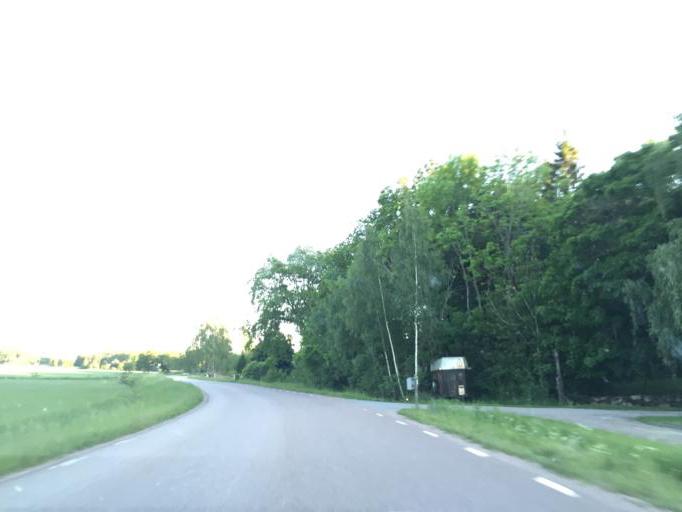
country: SE
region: Soedermanland
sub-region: Eskilstuna Kommun
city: Torshalla
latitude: 59.5172
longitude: 16.4368
